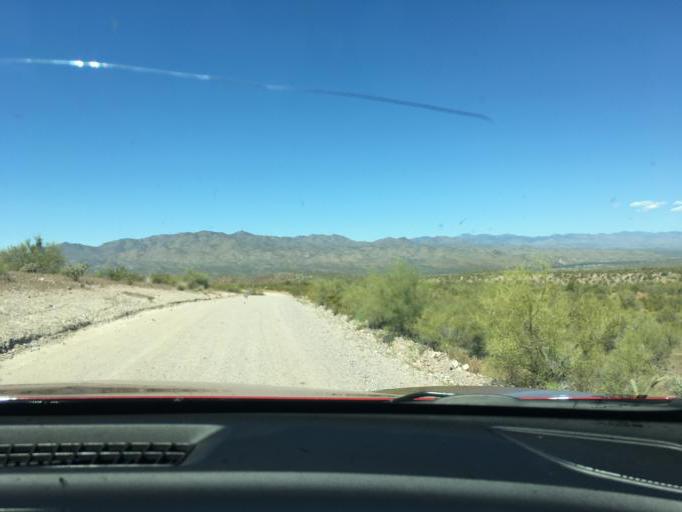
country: US
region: Arizona
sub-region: Yavapai County
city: Bagdad
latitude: 34.6109
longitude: -113.5167
